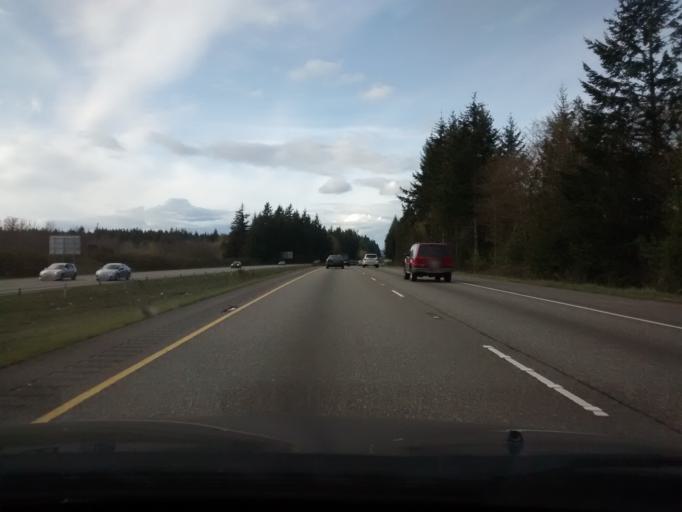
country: US
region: Washington
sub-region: Pierce County
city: Gig Harbor
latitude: 47.3371
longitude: -122.6045
